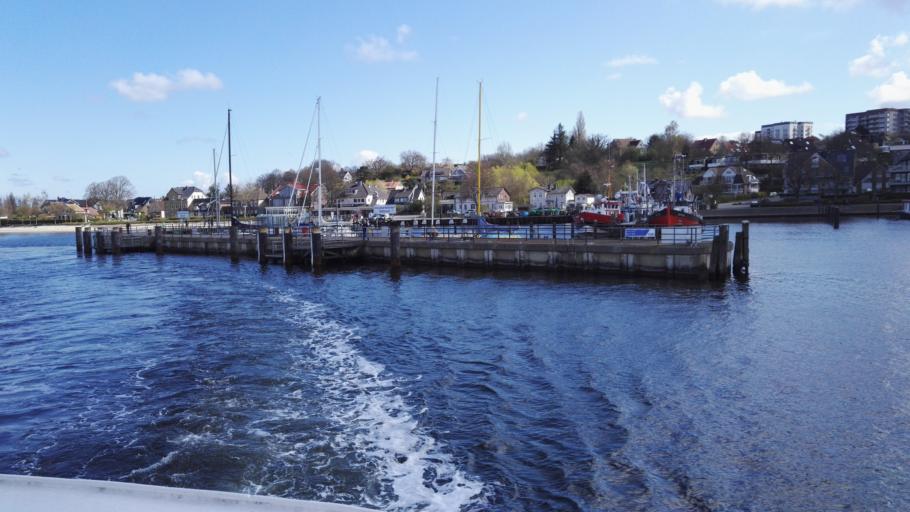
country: DE
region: Schleswig-Holstein
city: Heikendorf
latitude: 54.3752
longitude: 10.1941
